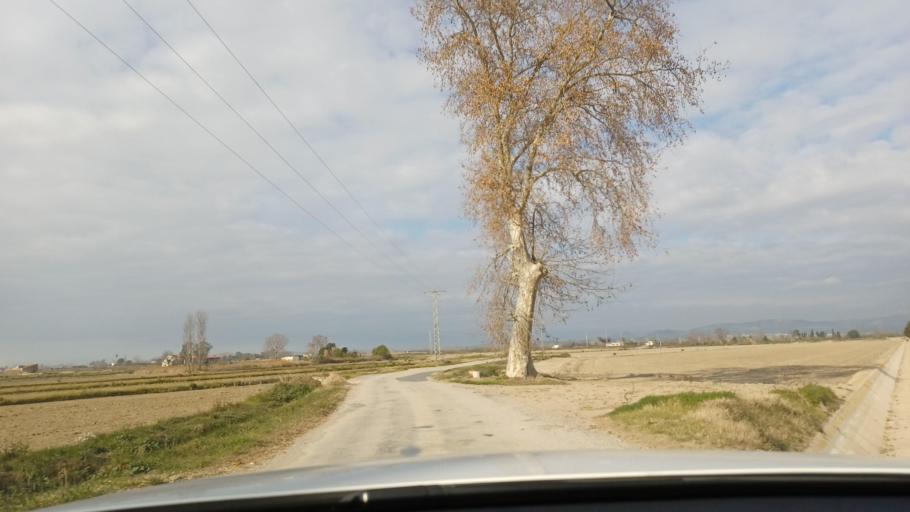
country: ES
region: Catalonia
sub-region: Provincia de Tarragona
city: Amposta
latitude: 40.7022
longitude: 0.6385
